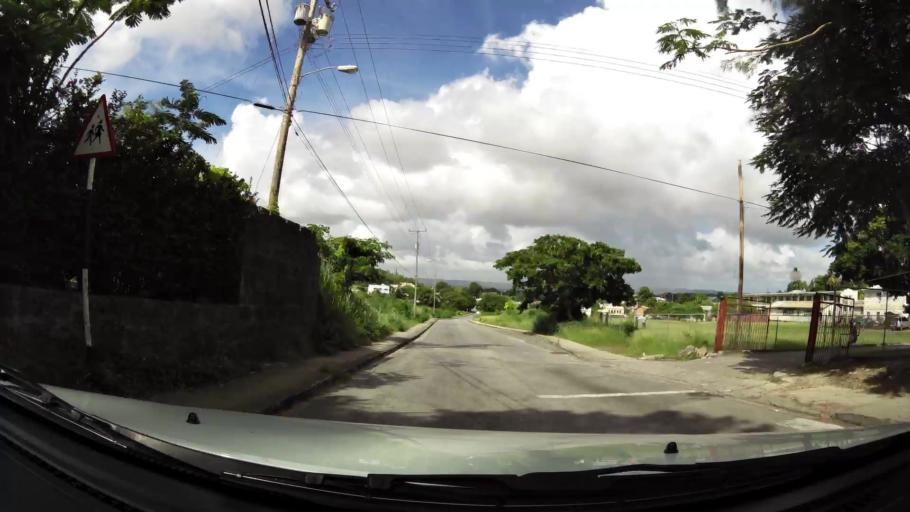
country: BB
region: Saint Michael
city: Bridgetown
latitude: 13.0954
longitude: -59.5933
